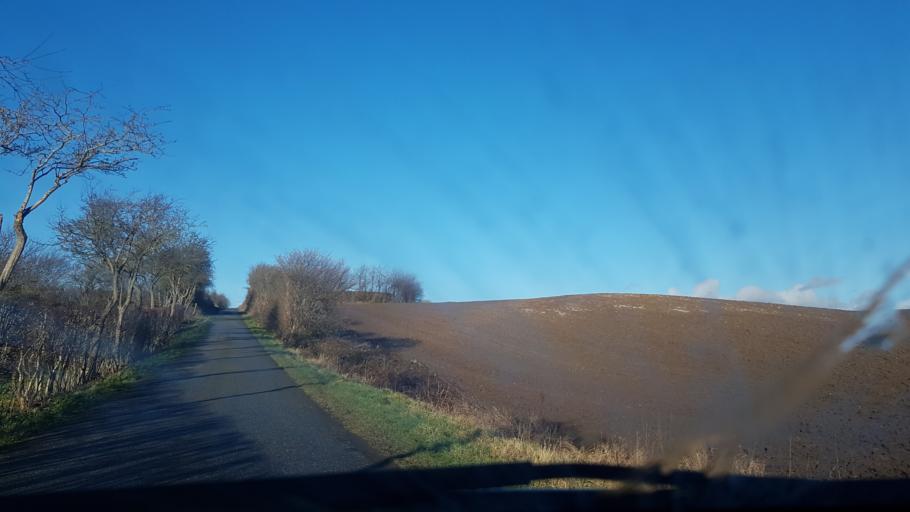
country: DK
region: South Denmark
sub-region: Fredericia Kommune
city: Taulov
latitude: 55.5283
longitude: 9.6454
